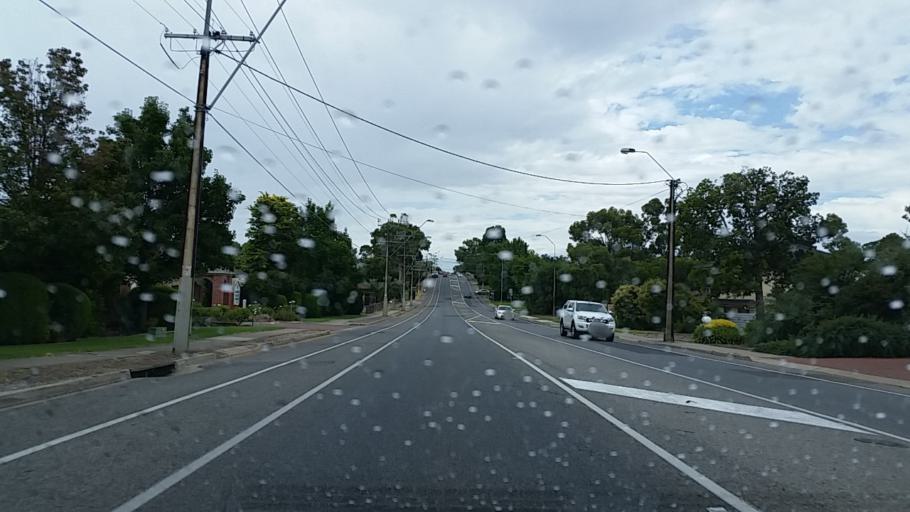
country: AU
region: South Australia
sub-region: Tea Tree Gully
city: Modbury
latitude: -34.8424
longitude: 138.6888
